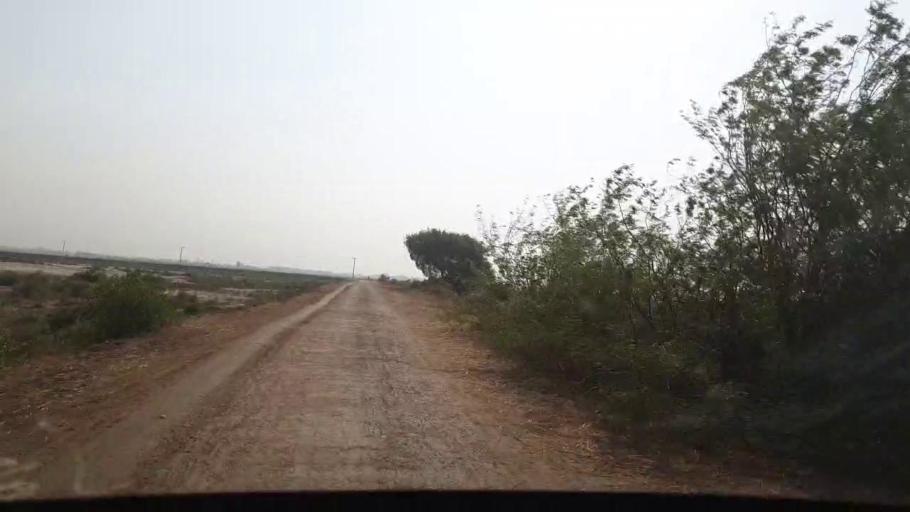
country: PK
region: Sindh
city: Chuhar Jamali
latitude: 24.3729
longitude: 67.9439
